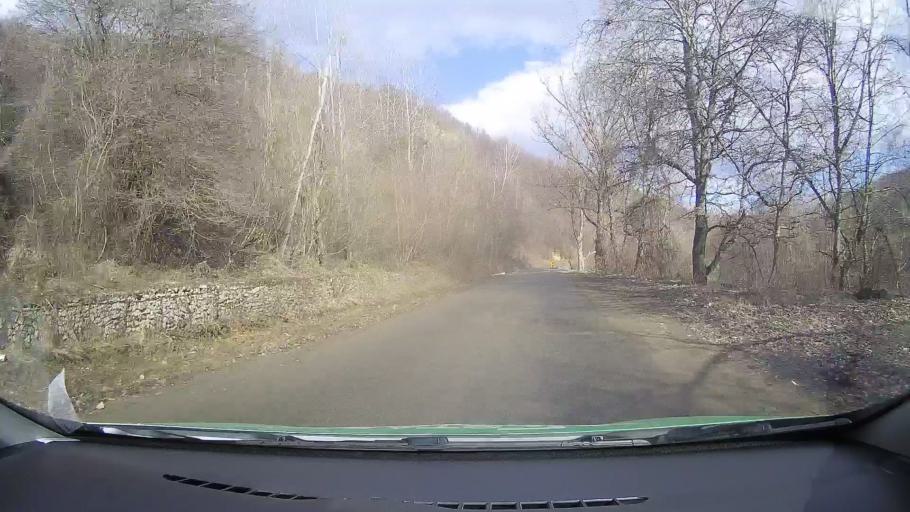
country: RO
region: Dambovita
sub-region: Comuna Motaeni
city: Motaeni
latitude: 45.1018
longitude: 25.4404
